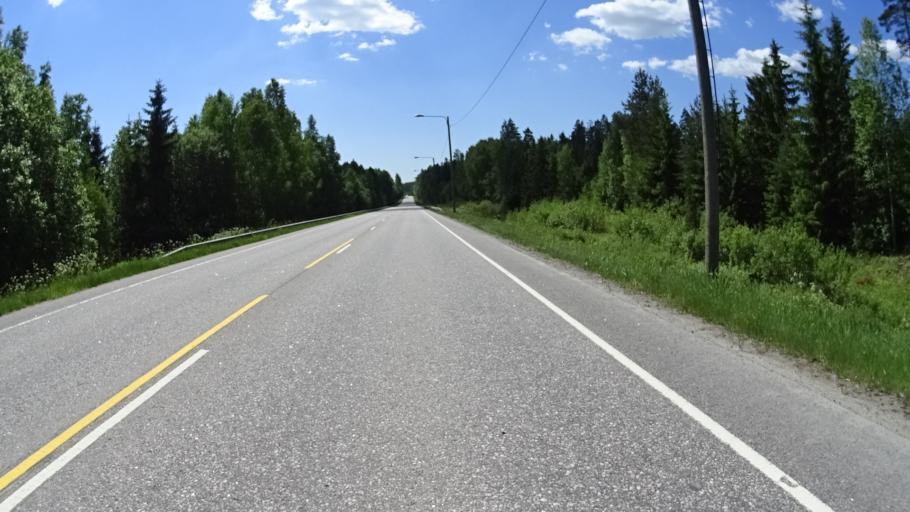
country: FI
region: Uusimaa
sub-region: Helsinki
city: Nurmijaervi
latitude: 60.3810
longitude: 24.8070
